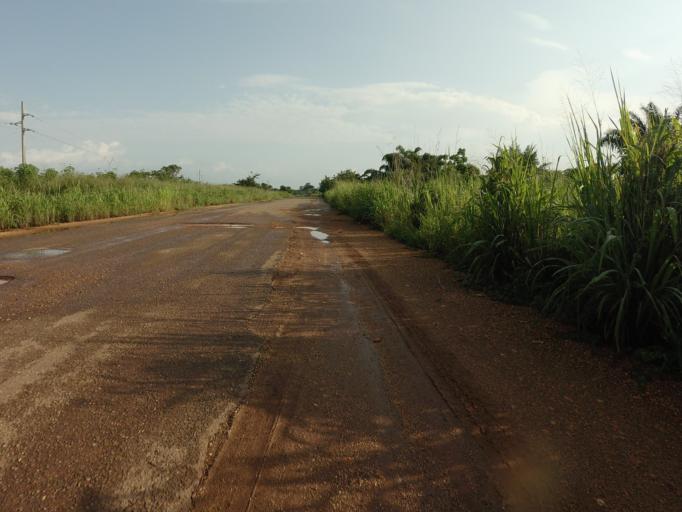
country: GH
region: Volta
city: Hohoe
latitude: 7.0746
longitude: 0.4370
